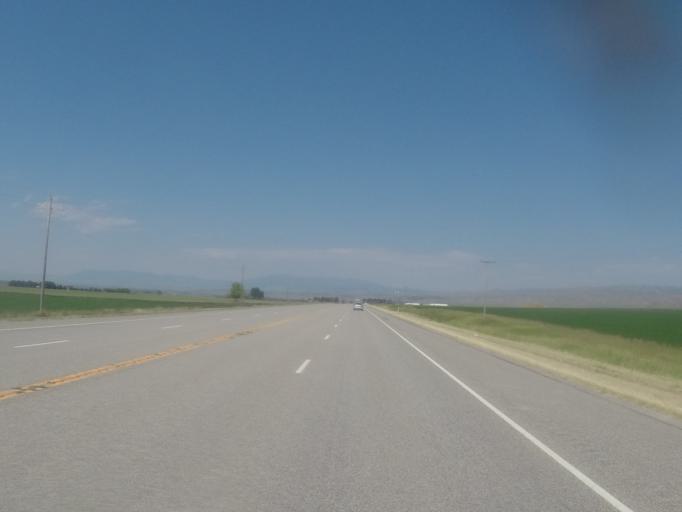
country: US
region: Montana
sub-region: Broadwater County
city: Townsend
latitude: 46.1263
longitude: -111.4917
